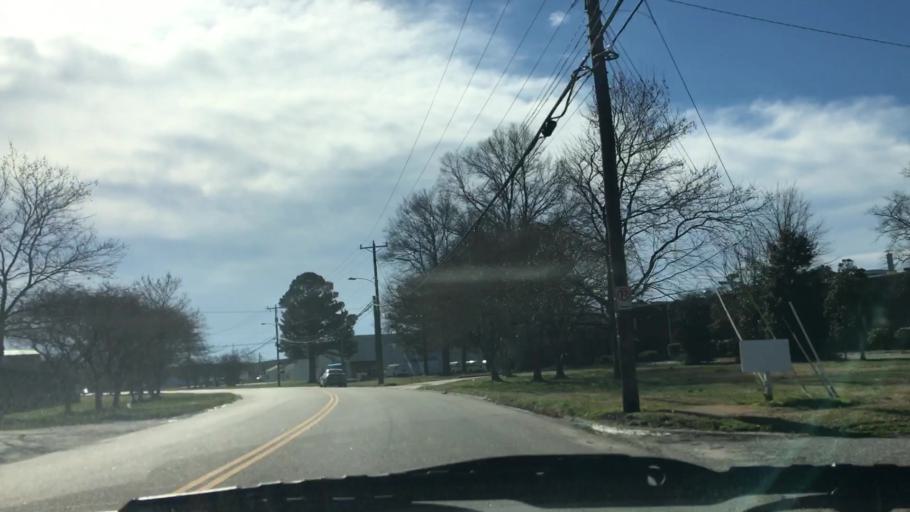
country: US
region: Virginia
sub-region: City of Norfolk
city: Norfolk
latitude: 36.8649
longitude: -76.2355
